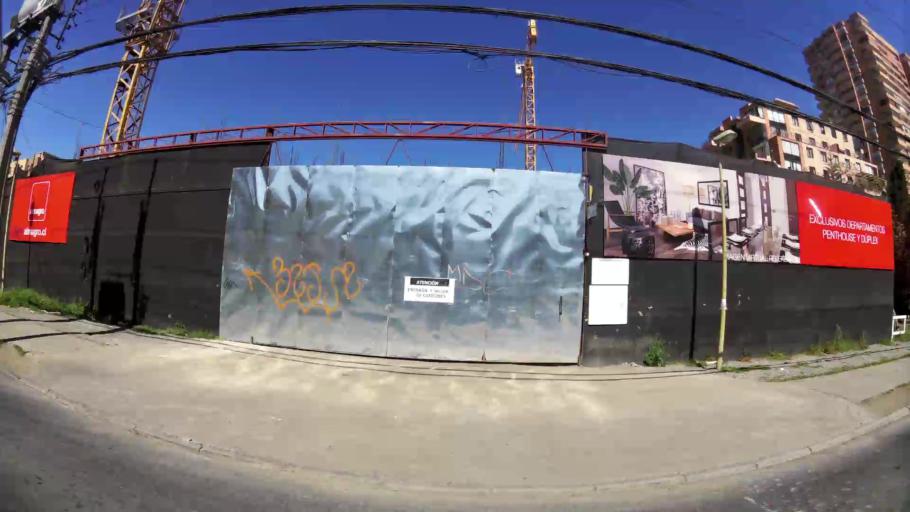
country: CL
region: Santiago Metropolitan
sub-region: Provincia de Santiago
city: Villa Presidente Frei, Nunoa, Santiago, Chile
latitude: -33.4115
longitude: -70.5686
